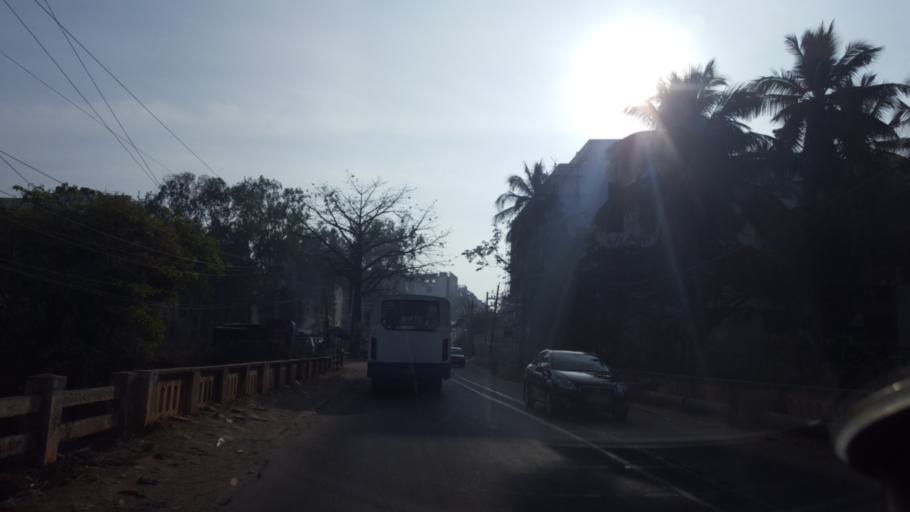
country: IN
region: Karnataka
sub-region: Bangalore Urban
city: Bangalore
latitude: 12.9040
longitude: 77.5109
